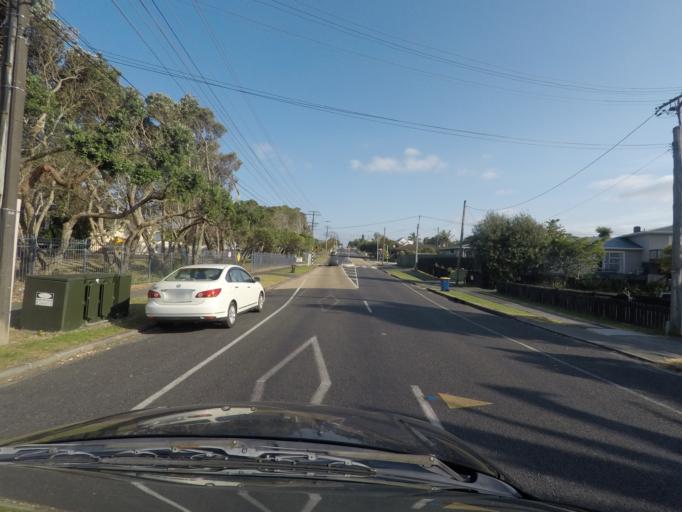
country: NZ
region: Auckland
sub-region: Auckland
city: Rosebank
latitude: -36.8603
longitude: 174.6445
